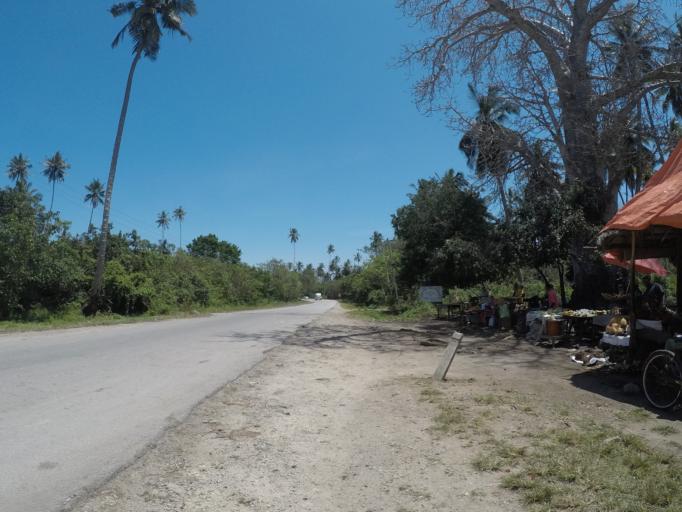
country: TZ
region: Zanzibar Central/South
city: Nganane
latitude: -6.2720
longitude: 39.4205
